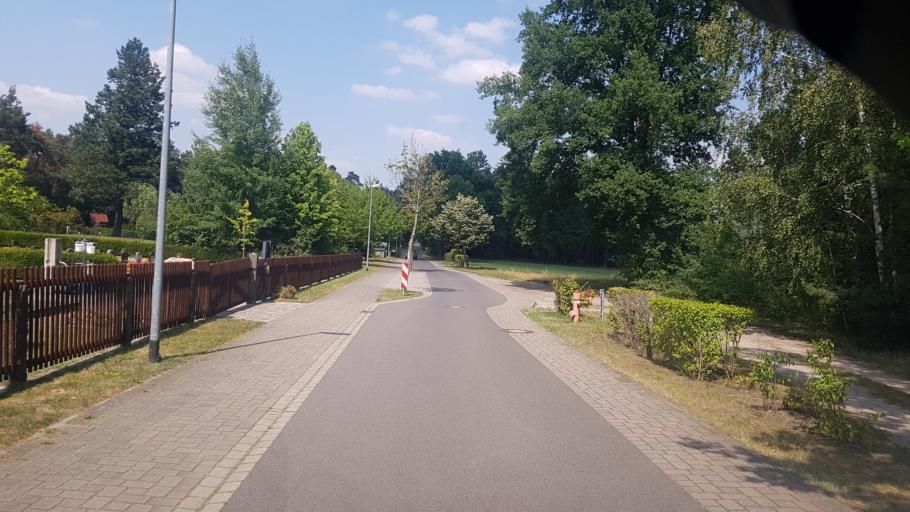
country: DE
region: Brandenburg
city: Spremberg
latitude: 51.6103
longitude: 14.3998
